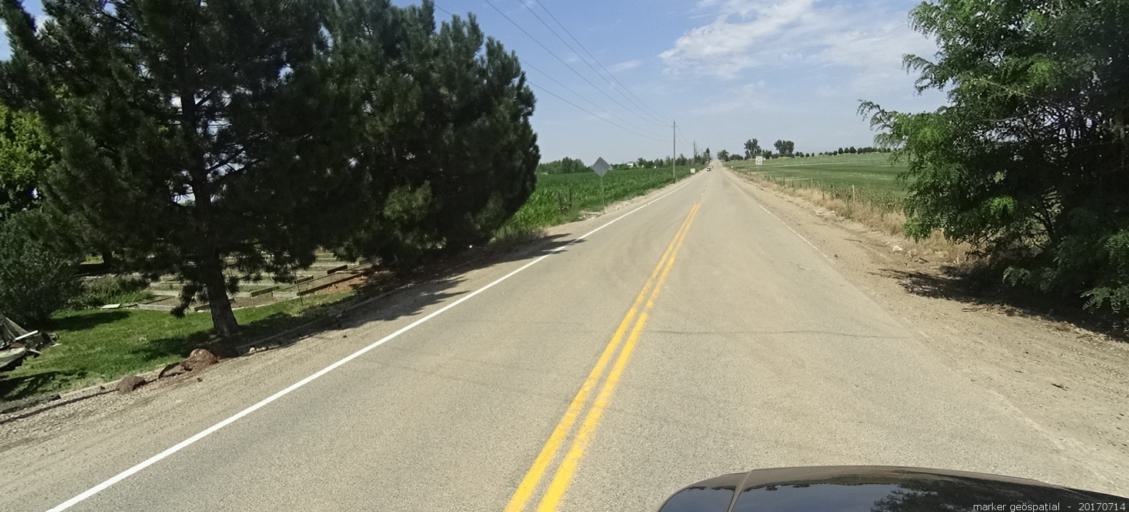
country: US
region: Idaho
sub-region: Ada County
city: Kuna
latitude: 43.5328
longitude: -116.3543
